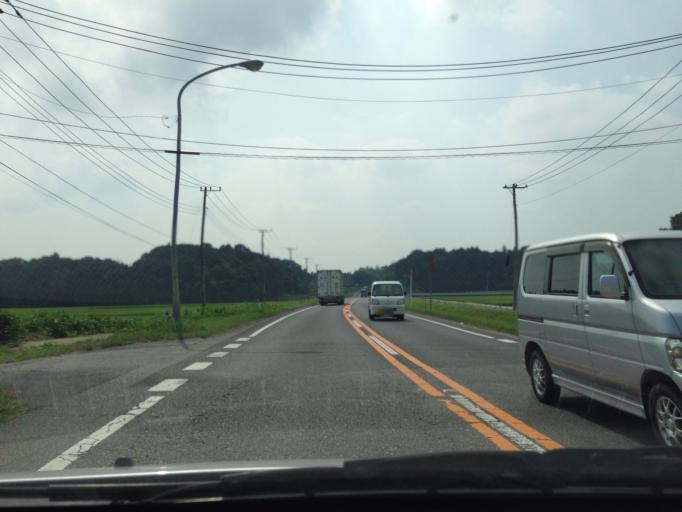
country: JP
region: Ibaraki
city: Inashiki
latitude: 36.0187
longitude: 140.2827
